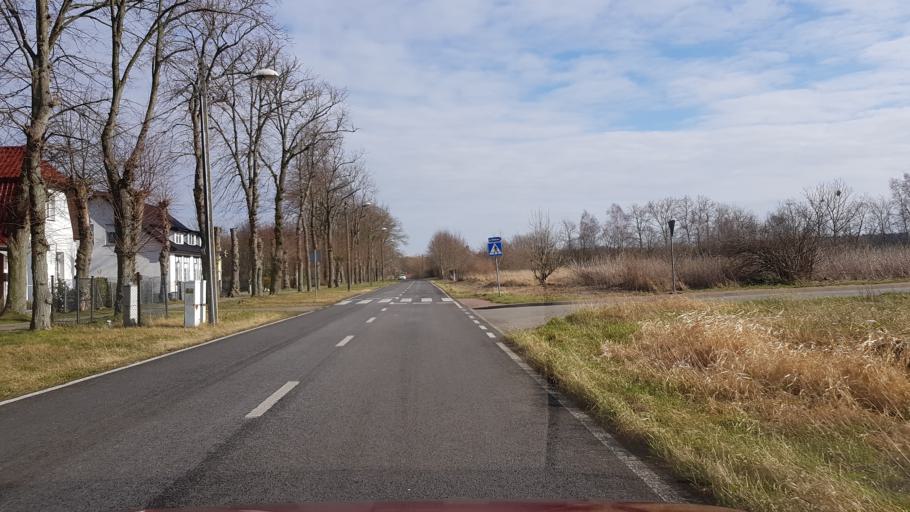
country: PL
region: West Pomeranian Voivodeship
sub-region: Powiat policki
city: Nowe Warpno
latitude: 53.7225
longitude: 14.2976
